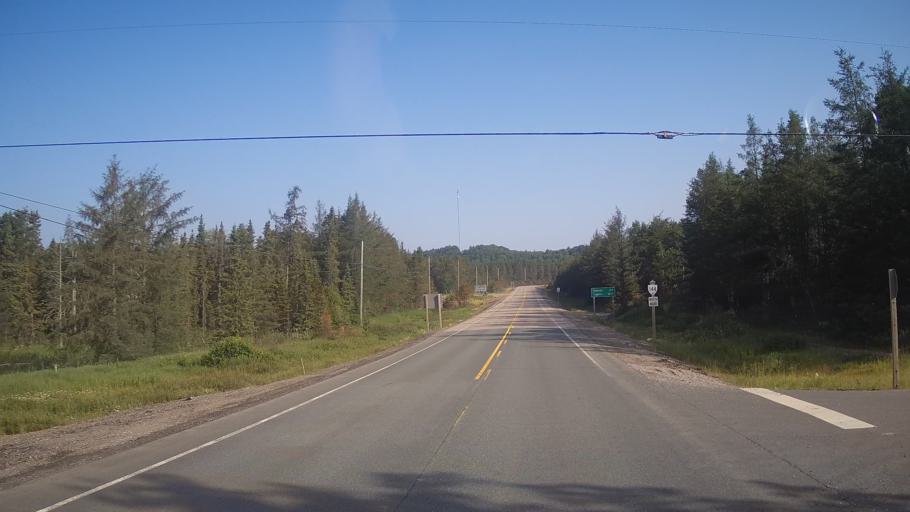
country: CA
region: Ontario
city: Rayside-Balfour
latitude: 46.7040
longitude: -81.5584
